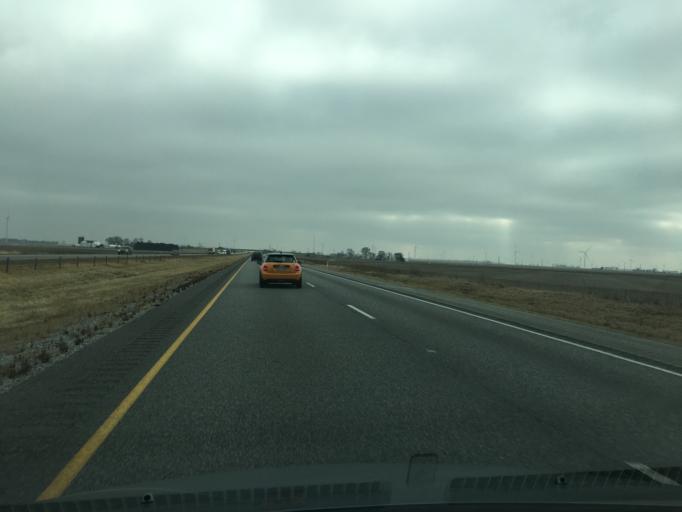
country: US
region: Indiana
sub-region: White County
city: Wolcott
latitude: 40.7151
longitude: -87.0767
